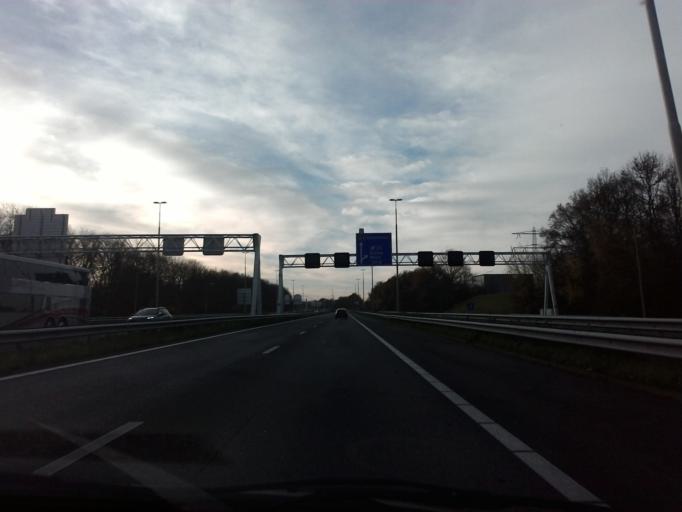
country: NL
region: Limburg
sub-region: Gemeente Stein
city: Stein
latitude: 50.9634
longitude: 5.7867
